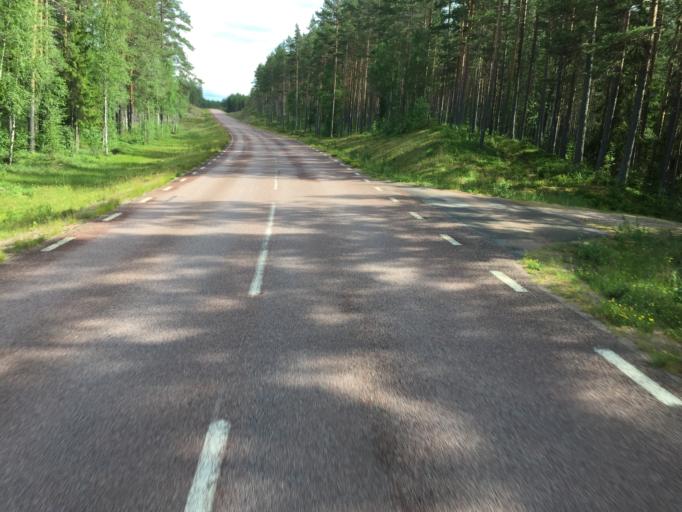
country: SE
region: Dalarna
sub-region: Vansbro Kommun
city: Vansbro
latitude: 60.6125
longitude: 14.1552
